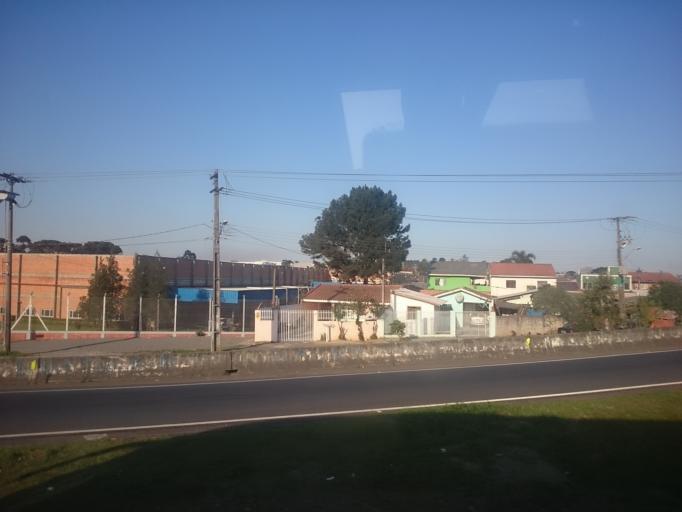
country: BR
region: Parana
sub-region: Sao Jose Dos Pinhais
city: Sao Jose dos Pinhais
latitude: -25.5416
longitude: -49.3026
